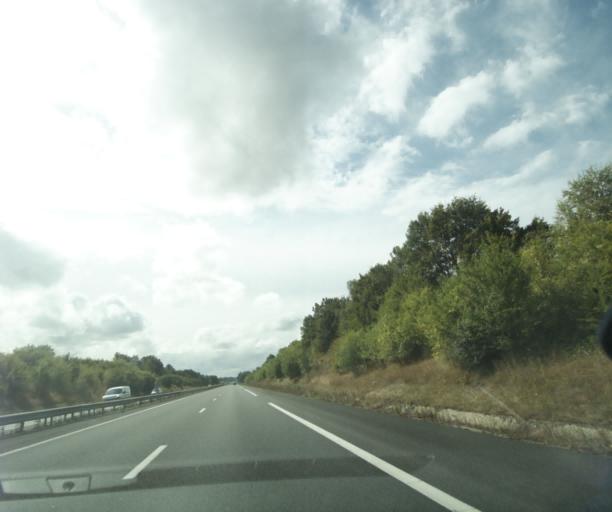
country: FR
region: Poitou-Charentes
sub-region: Departement de la Charente-Maritime
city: Pons
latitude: 45.5699
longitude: -0.6009
